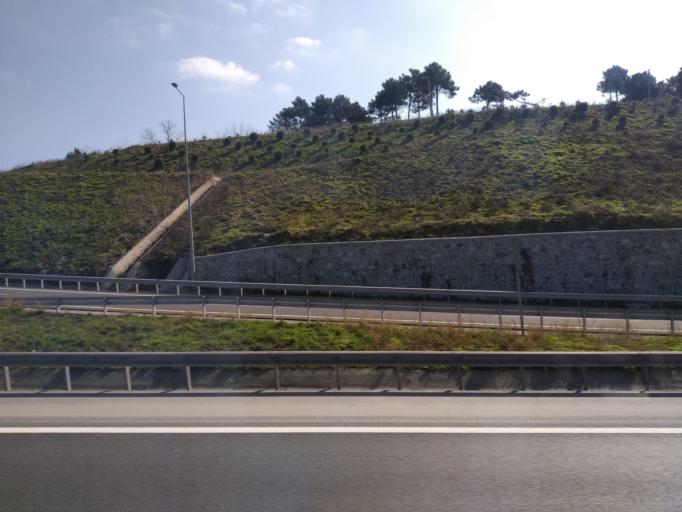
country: TR
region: Istanbul
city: Arikoey
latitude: 41.2245
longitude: 29.0169
